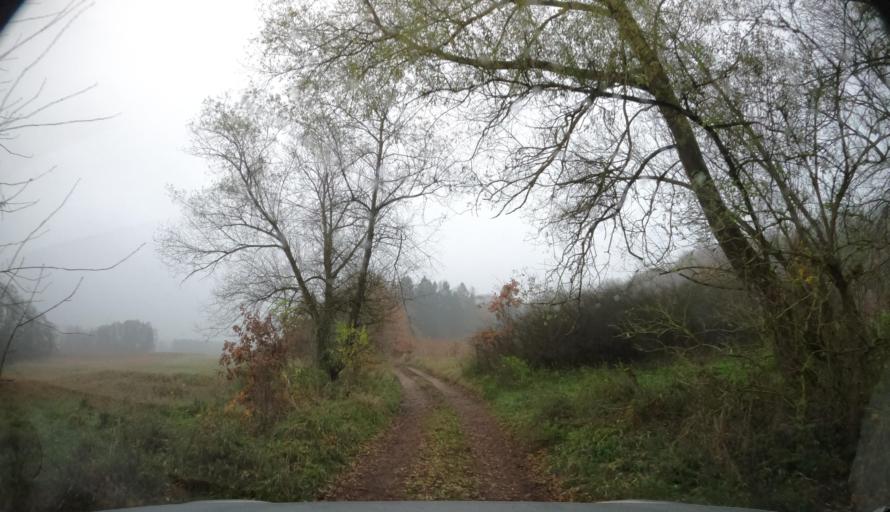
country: PL
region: West Pomeranian Voivodeship
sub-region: Powiat lobeski
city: Radowo Male
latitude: 53.6483
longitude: 15.5290
